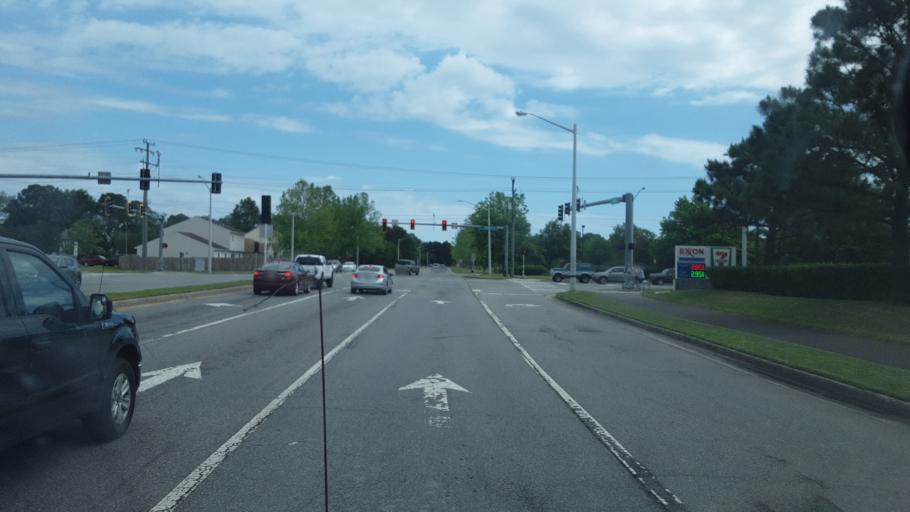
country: US
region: Virginia
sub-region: City of Virginia Beach
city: Virginia Beach
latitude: 36.7604
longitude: -76.0053
